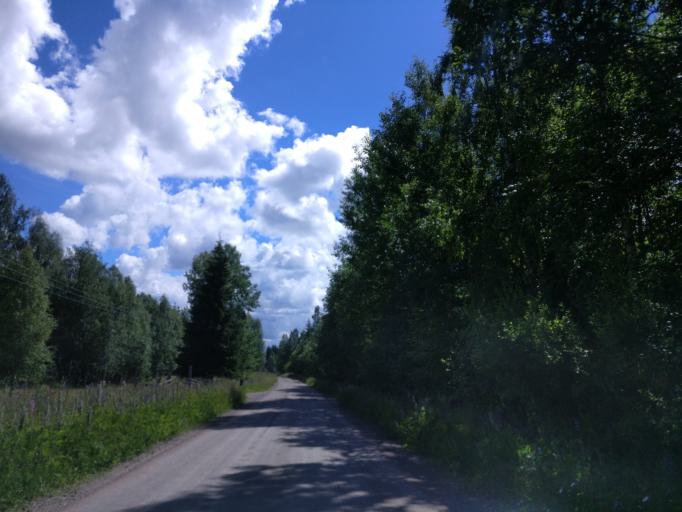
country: SE
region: Vaermland
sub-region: Hagfors Kommun
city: Hagfors
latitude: 60.0421
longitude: 13.6625
